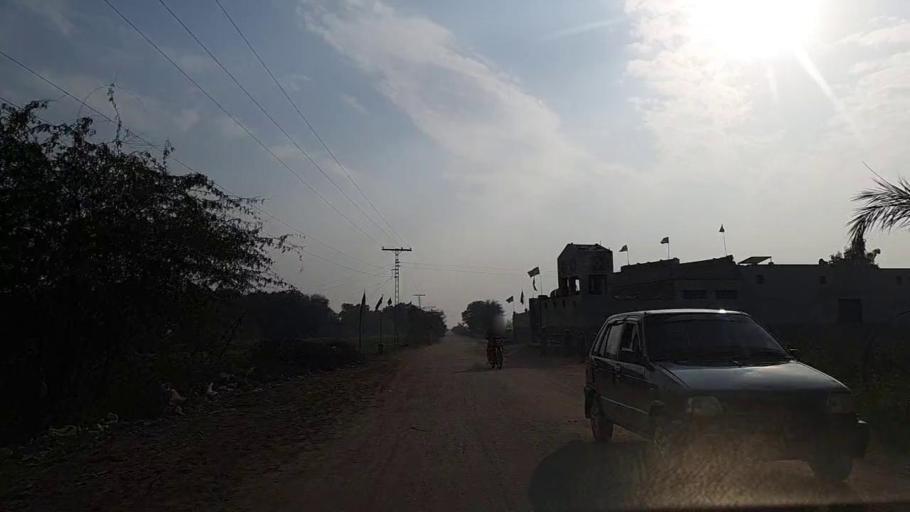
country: PK
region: Sindh
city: Jam Sahib
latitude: 26.3298
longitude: 68.5344
